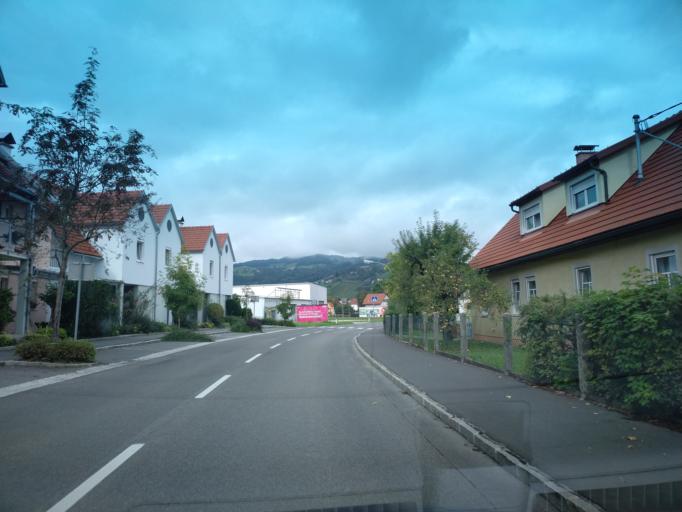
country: AT
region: Styria
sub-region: Politischer Bezirk Deutschlandsberg
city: Deutschlandsberg
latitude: 46.8139
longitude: 15.2231
